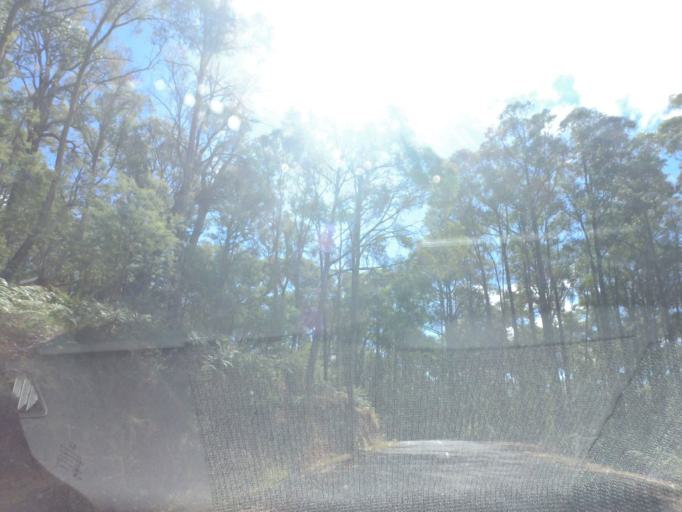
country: AU
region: Victoria
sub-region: Murrindindi
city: Alexandra
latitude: -37.3288
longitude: 145.9353
